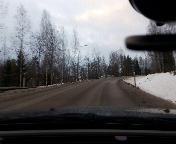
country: SE
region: Gaevleborg
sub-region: Bollnas Kommun
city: Bollnas
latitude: 61.3359
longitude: 16.3926
